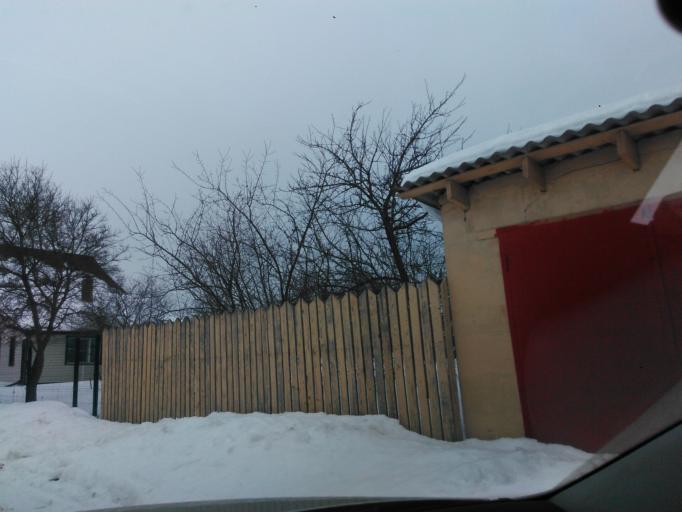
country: RU
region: Moskovskaya
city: Podosinki
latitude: 56.2703
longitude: 37.6239
